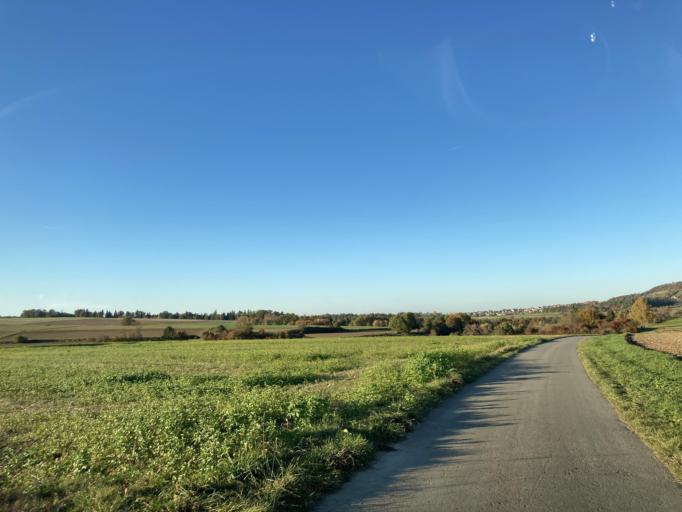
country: DE
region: Baden-Wuerttemberg
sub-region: Tuebingen Region
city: Hirrlingen
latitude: 48.4268
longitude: 8.9180
